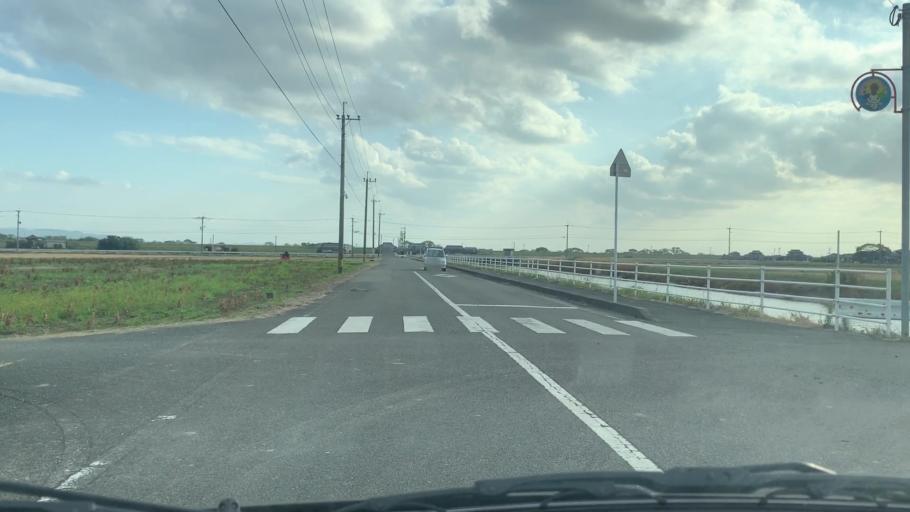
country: JP
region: Saga Prefecture
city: Kanzakimachi-kanzaki
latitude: 33.2813
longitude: 130.4411
